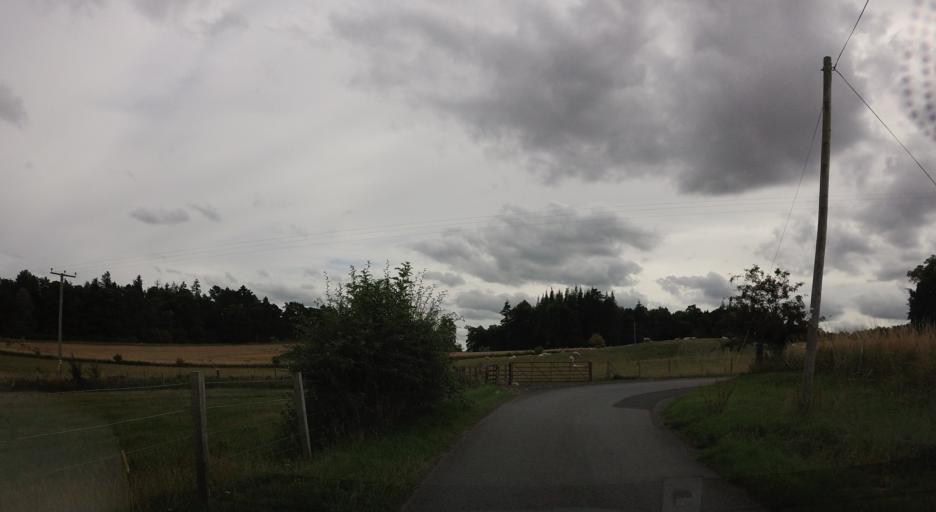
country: GB
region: Scotland
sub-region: Perth and Kinross
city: Bridge of Earn
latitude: 56.3663
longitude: -3.3614
